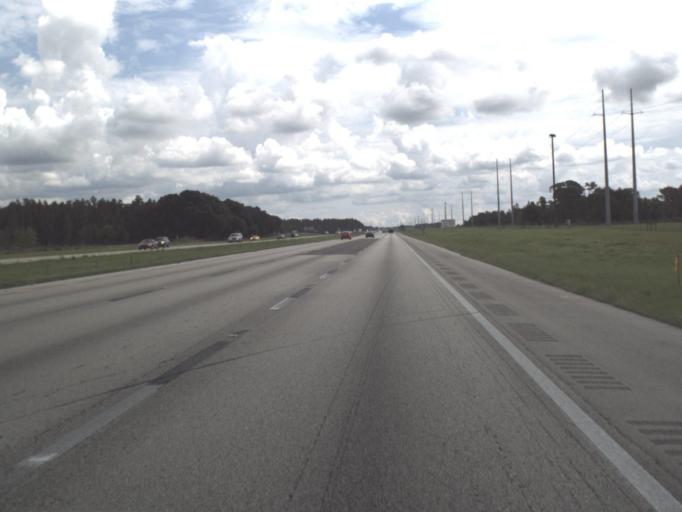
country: US
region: Florida
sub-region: Polk County
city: Polk City
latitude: 28.1440
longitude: -81.8840
